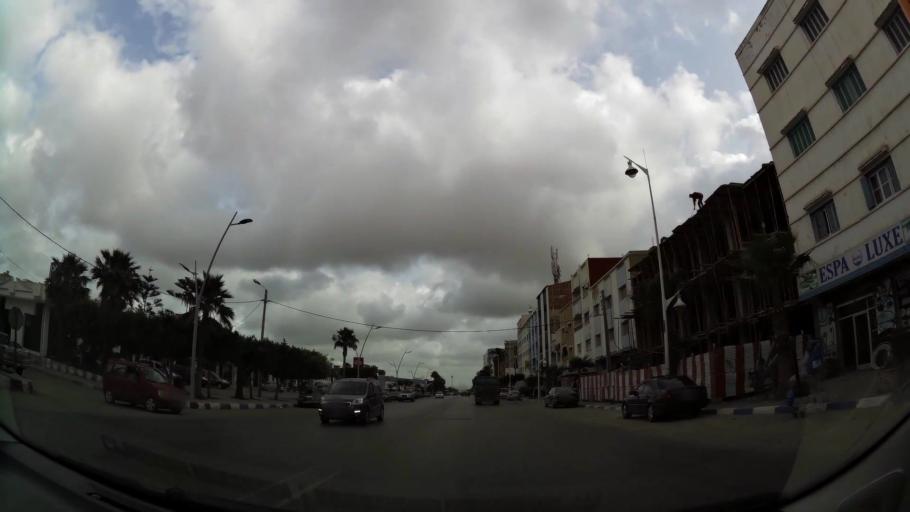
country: MA
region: Oriental
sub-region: Nador
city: Nador
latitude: 35.1556
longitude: -2.9295
